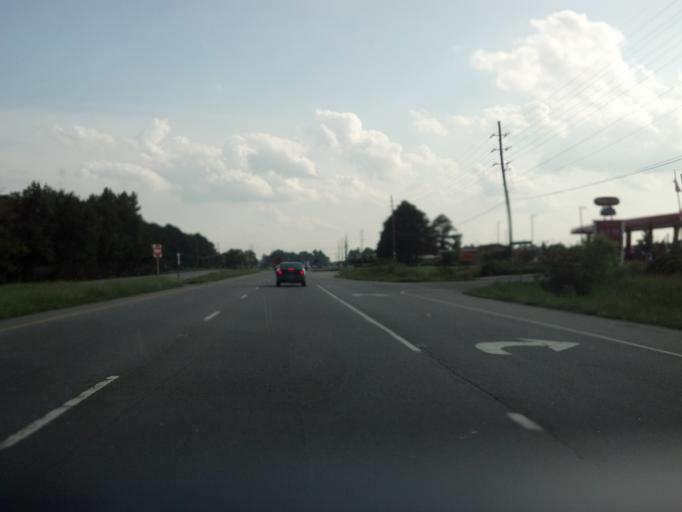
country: US
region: North Carolina
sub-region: Pitt County
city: Greenville
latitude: 35.6572
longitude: -77.3642
